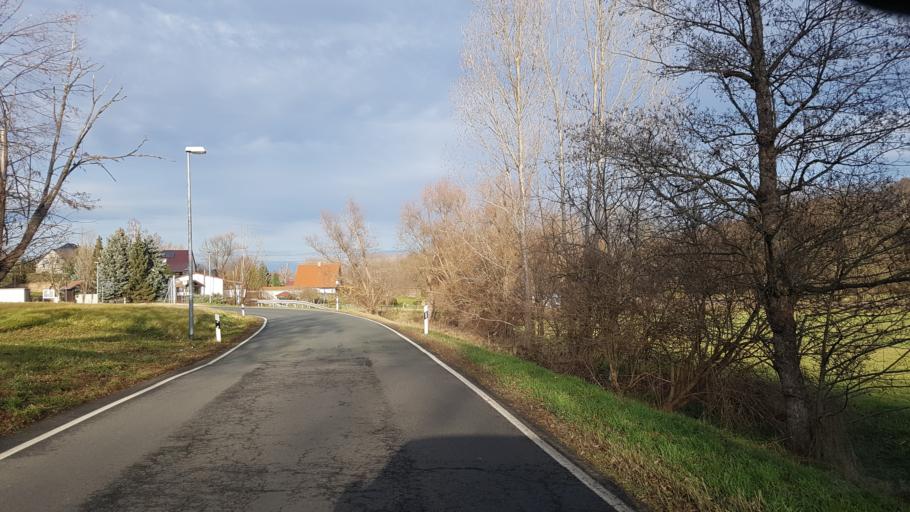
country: DE
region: Saxony
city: Ostrau
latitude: 51.1811
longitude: 13.1657
